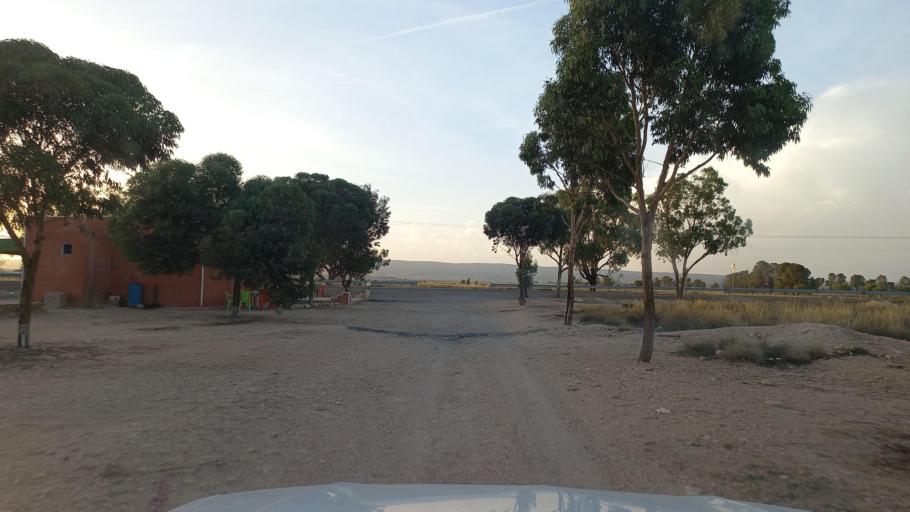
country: TN
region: Al Qasrayn
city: Kasserine
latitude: 35.2424
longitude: 8.9919
